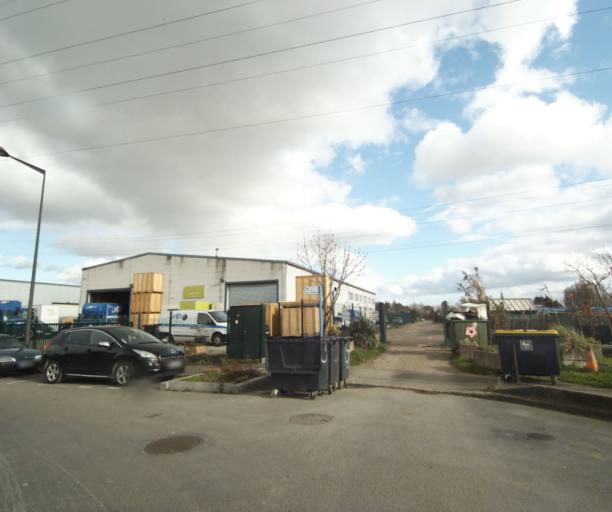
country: FR
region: Ile-de-France
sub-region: Departement de Seine-Saint-Denis
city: Villetaneuse
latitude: 48.9559
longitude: 2.3482
